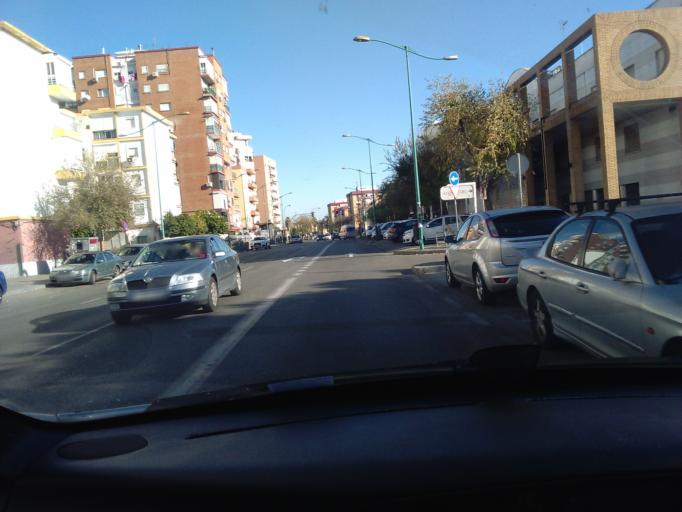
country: ES
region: Andalusia
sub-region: Provincia de Sevilla
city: Sevilla
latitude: 37.4076
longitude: -5.9872
